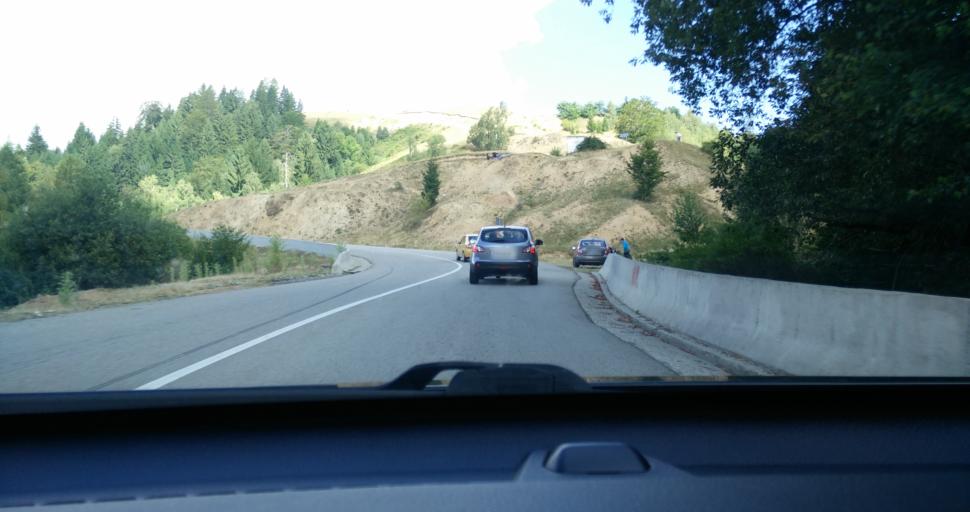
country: RO
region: Gorj
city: Novaci-Straini
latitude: 45.2243
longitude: 23.6960
